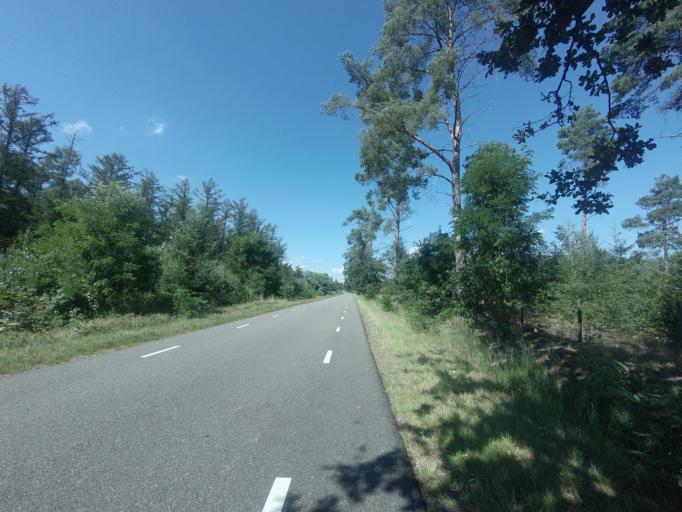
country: NL
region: Overijssel
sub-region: Gemeente Twenterand
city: Den Ham
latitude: 52.5464
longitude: 6.4416
